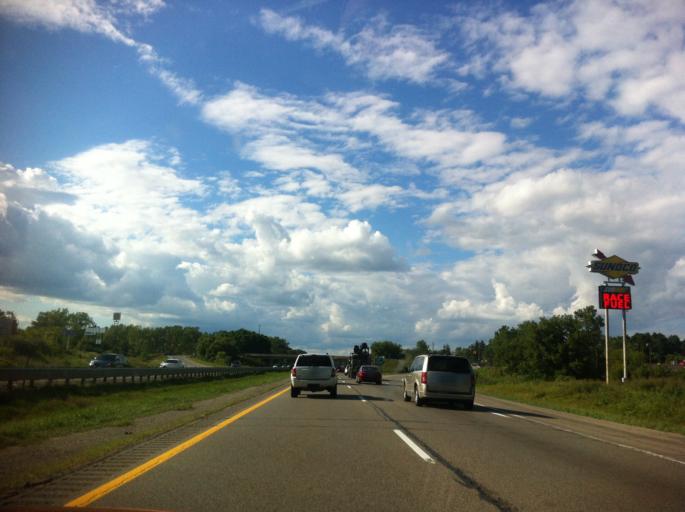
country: US
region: Michigan
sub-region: Livingston County
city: Whitmore Lake
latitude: 42.3764
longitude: -83.7551
